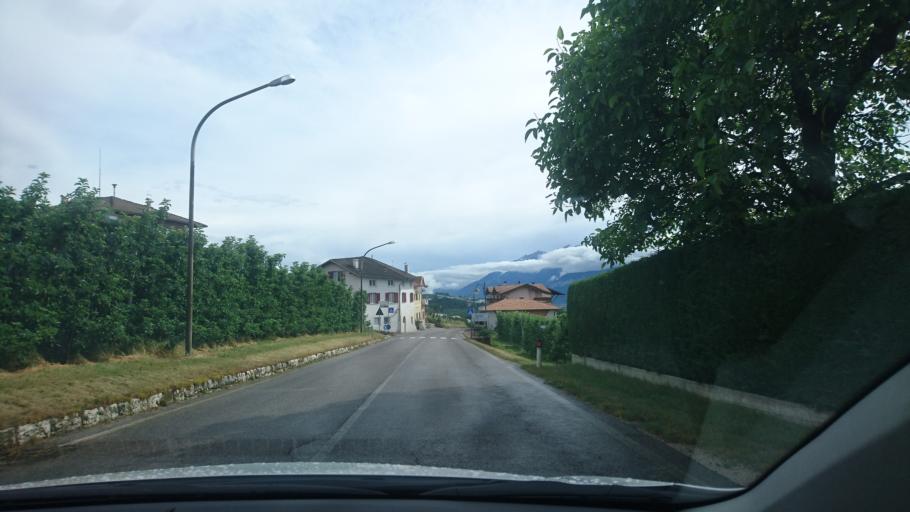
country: IT
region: Trentino-Alto Adige
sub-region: Provincia di Trento
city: Sanzeno
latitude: 46.3796
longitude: 11.0894
